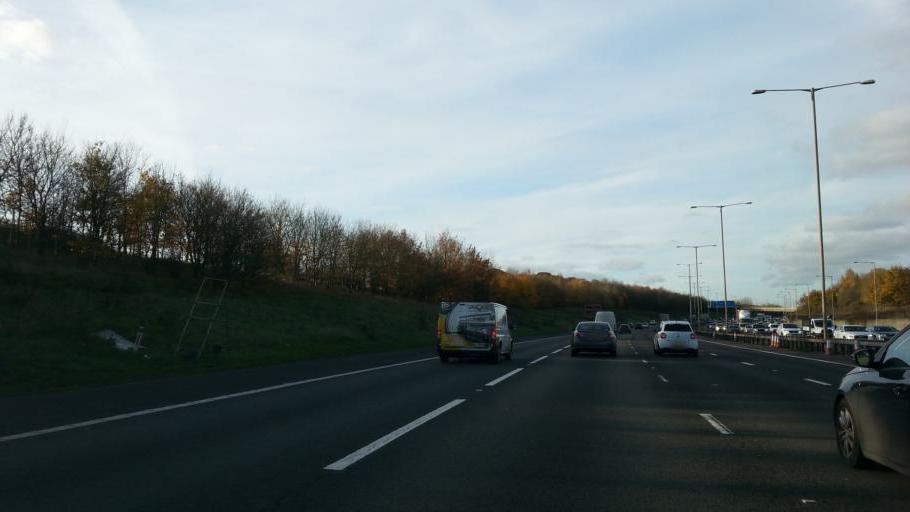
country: GB
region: England
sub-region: Buckinghamshire
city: Denham
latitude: 51.5485
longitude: -0.5184
